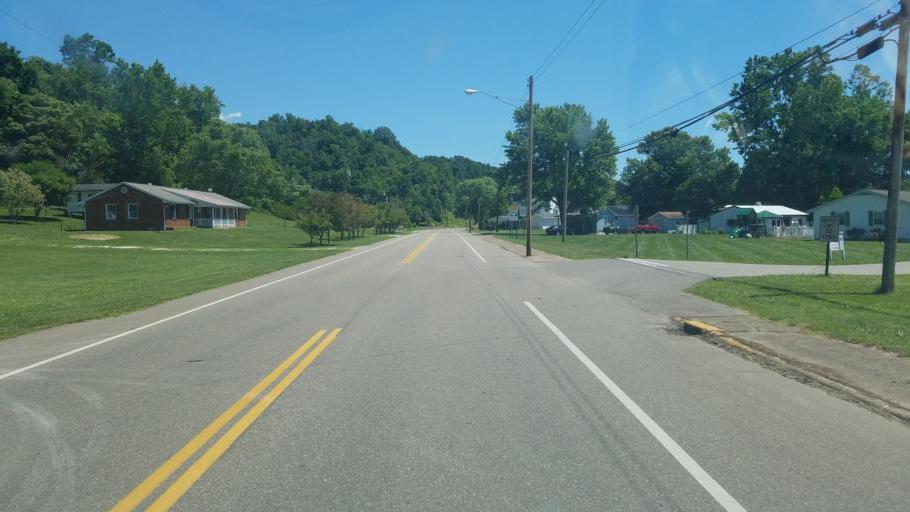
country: US
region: West Virginia
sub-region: Cabell County
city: Lesage
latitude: 38.5907
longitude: -82.2860
